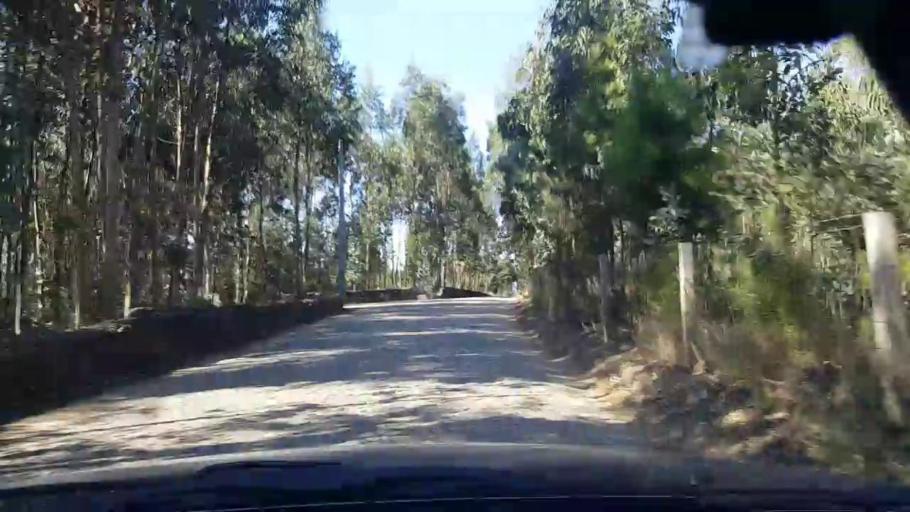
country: PT
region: Braga
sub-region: Vila Nova de Famalicao
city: Ribeirao
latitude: 41.3916
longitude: -8.6366
